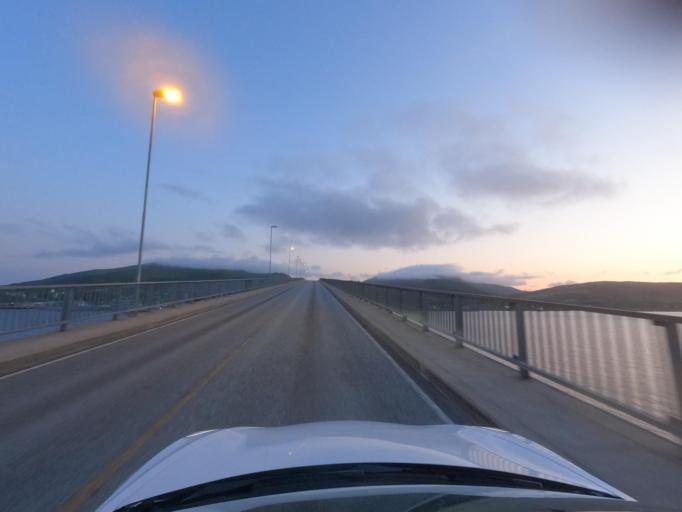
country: NO
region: Nordland
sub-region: Sortland
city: Sortland
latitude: 68.7067
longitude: 15.4338
